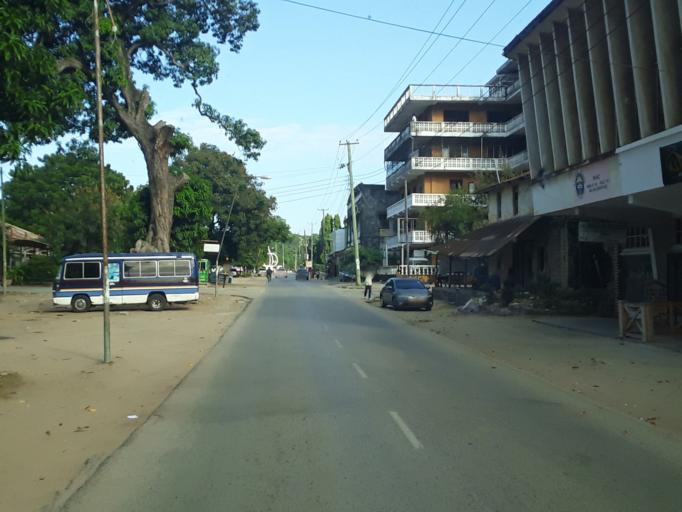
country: TZ
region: Tanga
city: Tanga
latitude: -5.0726
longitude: 39.1037
